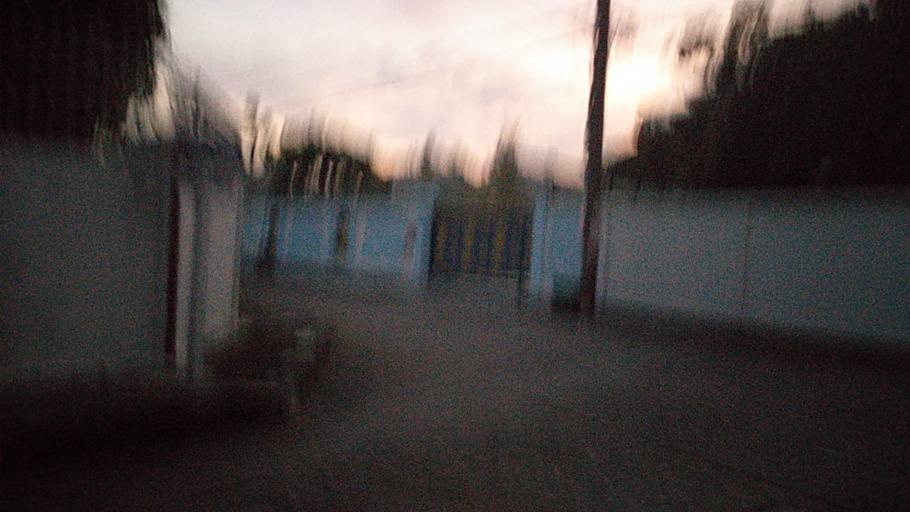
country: TH
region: Bangkok
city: Lat Phrao
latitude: 13.8283
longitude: 100.6107
